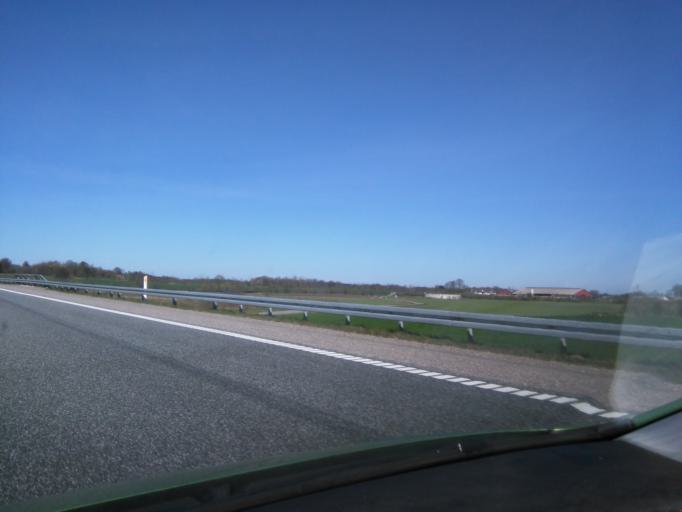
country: DK
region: South Denmark
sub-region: Vejle Kommune
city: Jelling
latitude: 55.8364
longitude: 9.3874
